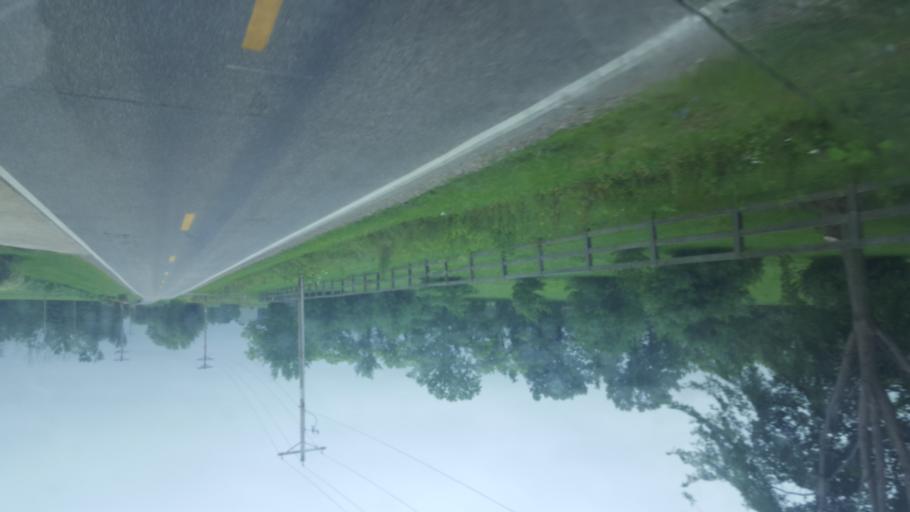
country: US
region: Ohio
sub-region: Delaware County
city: Sunbury
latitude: 40.2720
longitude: -82.8872
